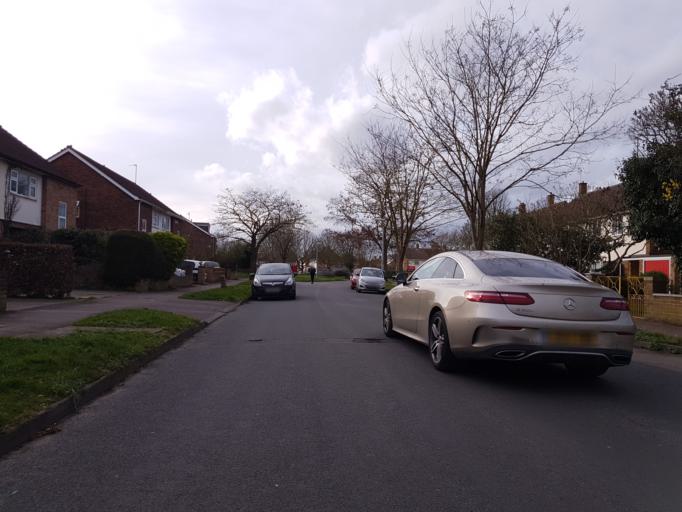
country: GB
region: England
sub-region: Cambridgeshire
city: Cambridge
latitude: 52.2230
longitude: 0.1175
